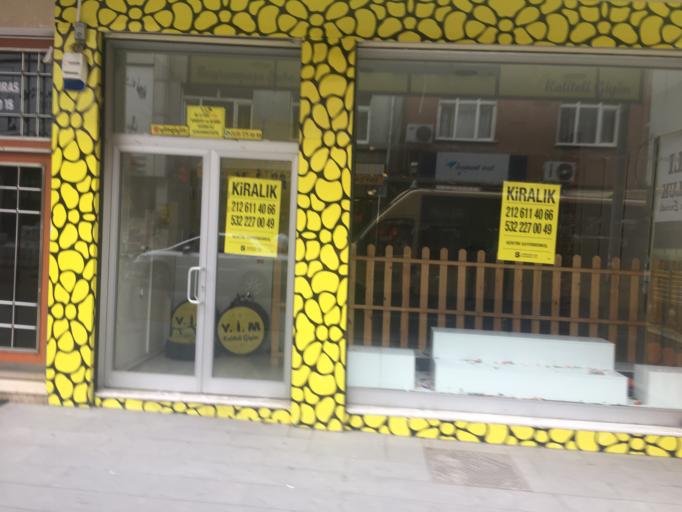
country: TR
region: Istanbul
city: Esenler
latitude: 41.0463
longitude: 28.9058
